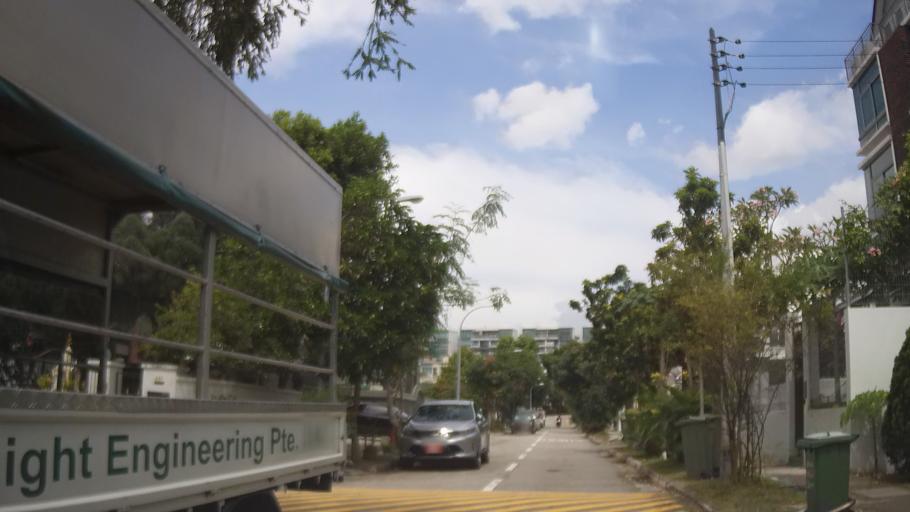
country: SG
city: Singapore
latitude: 1.3483
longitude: 103.8827
